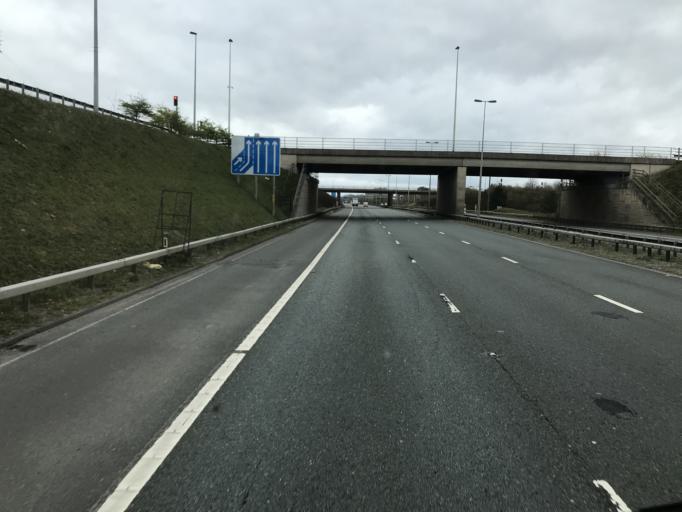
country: GB
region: England
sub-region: Warrington
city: Burtonwood
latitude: 53.4154
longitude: -2.6489
